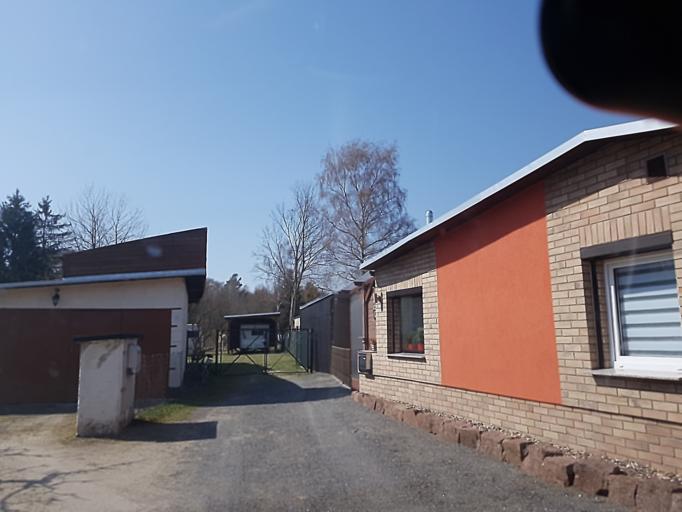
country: DE
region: Brandenburg
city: Finsterwalde
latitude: 51.6337
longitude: 13.6949
